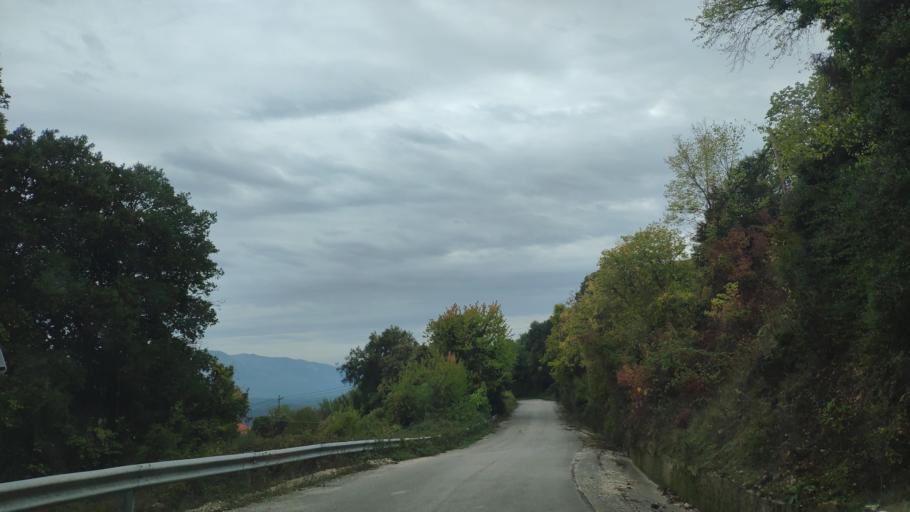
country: GR
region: Epirus
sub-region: Nomos Thesprotias
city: Paramythia
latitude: 39.4587
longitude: 20.6745
